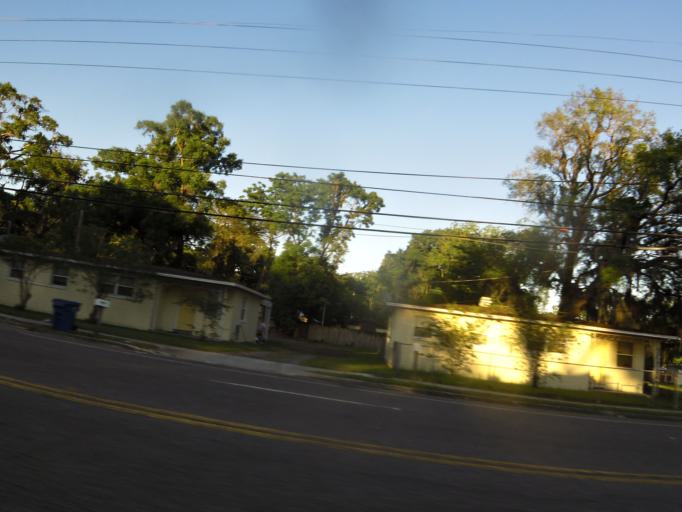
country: US
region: Florida
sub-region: Duval County
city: Jacksonville
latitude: 30.3163
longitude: -81.5793
